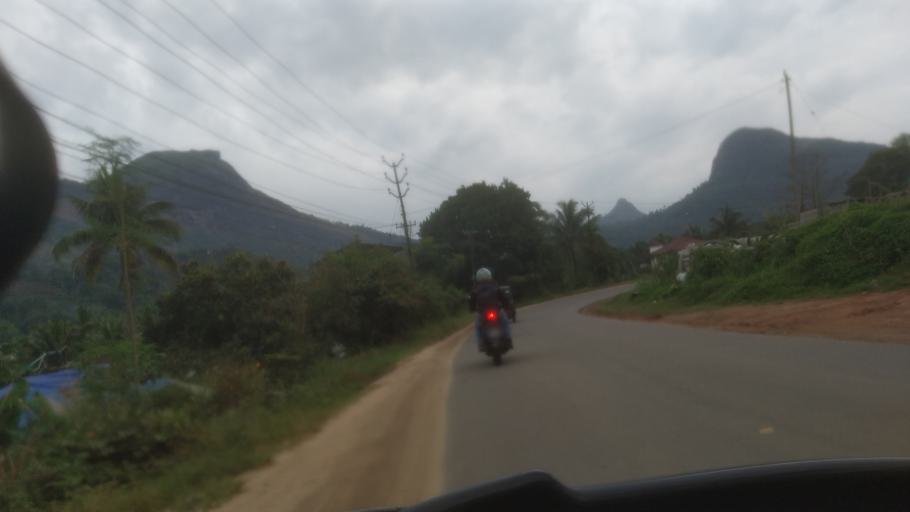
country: IN
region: Kerala
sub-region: Idukki
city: Munnar
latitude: 10.0070
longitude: 76.9621
